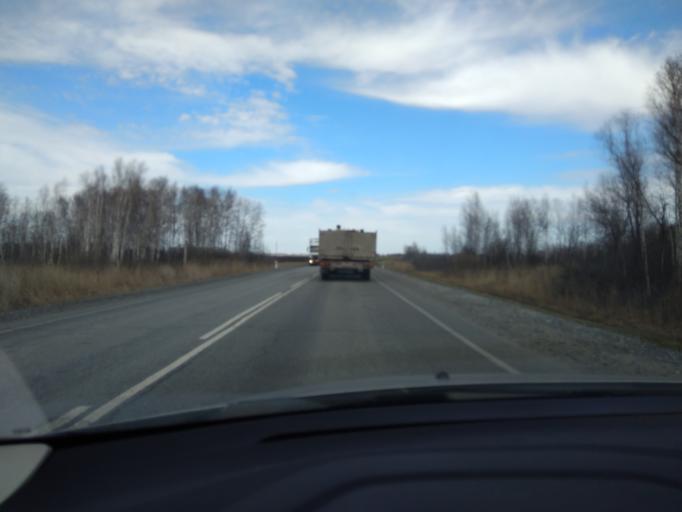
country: RU
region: Sverdlovsk
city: Pyshma
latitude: 56.9767
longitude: 63.2360
